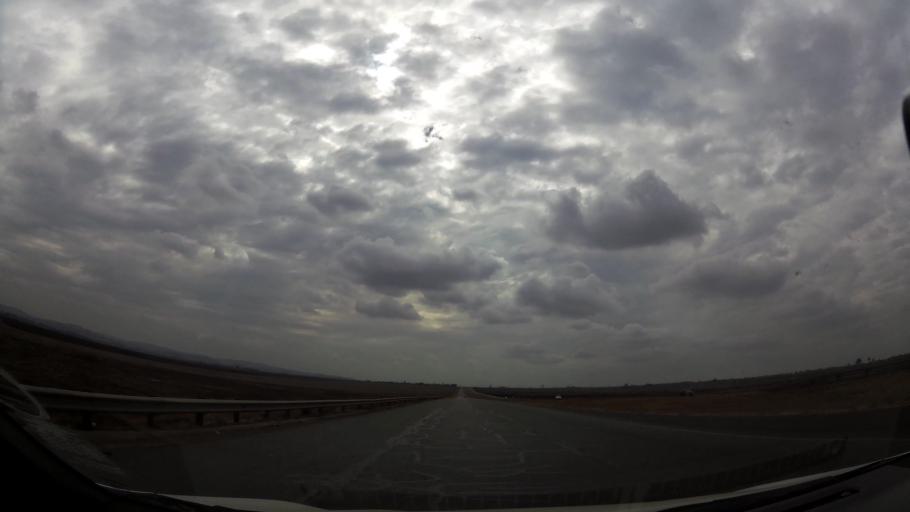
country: ZA
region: Gauteng
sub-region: Ekurhuleni Metropolitan Municipality
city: Germiston
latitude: -26.3796
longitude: 28.0885
